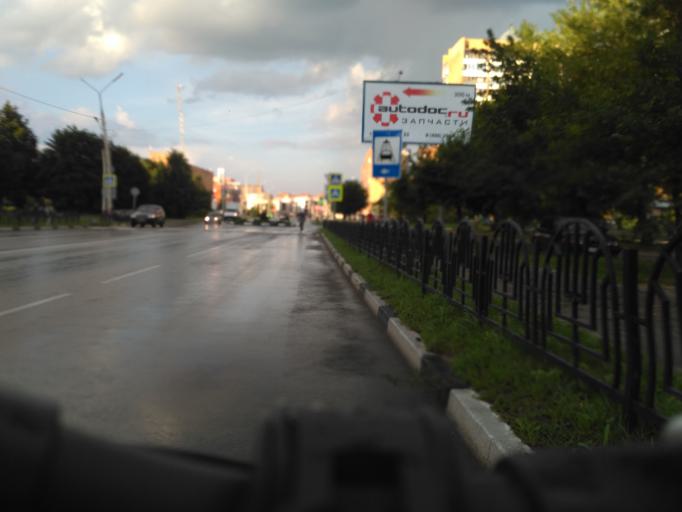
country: RU
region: Moskovskaya
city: Dubna
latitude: 56.7333
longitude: 37.1530
